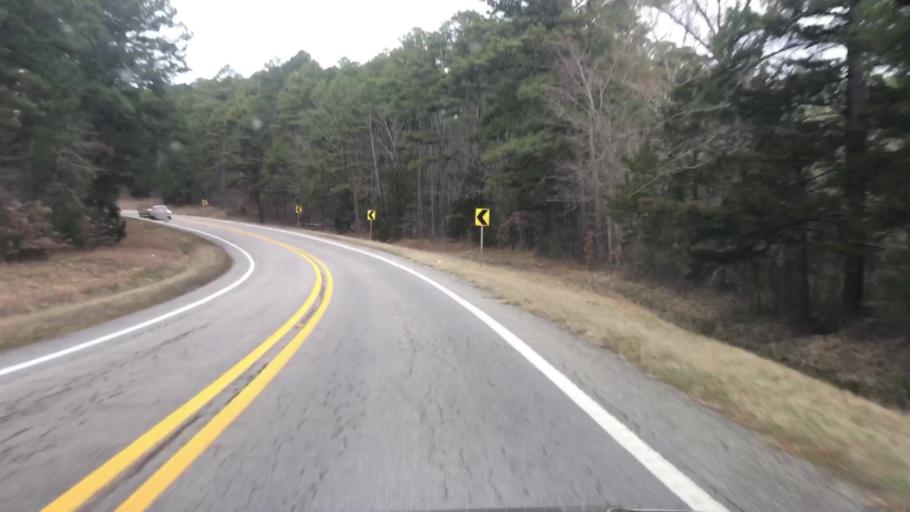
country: US
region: Arkansas
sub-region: Montgomery County
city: Mount Ida
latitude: 34.6702
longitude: -93.7775
